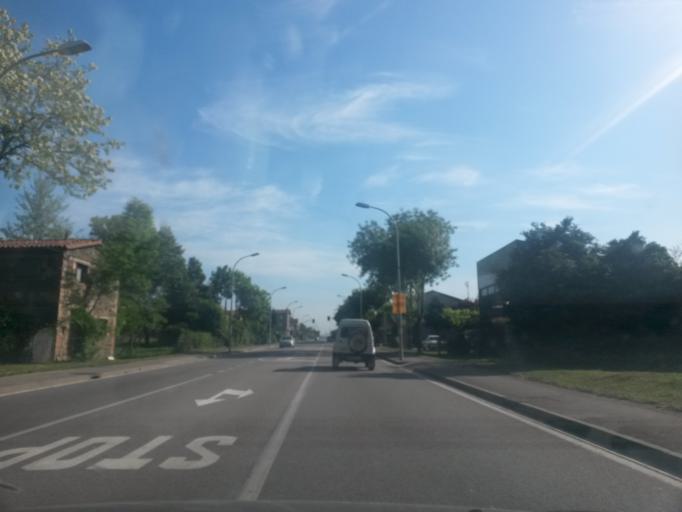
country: ES
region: Catalonia
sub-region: Provincia de Girona
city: Olot
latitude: 42.1590
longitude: 2.4674
